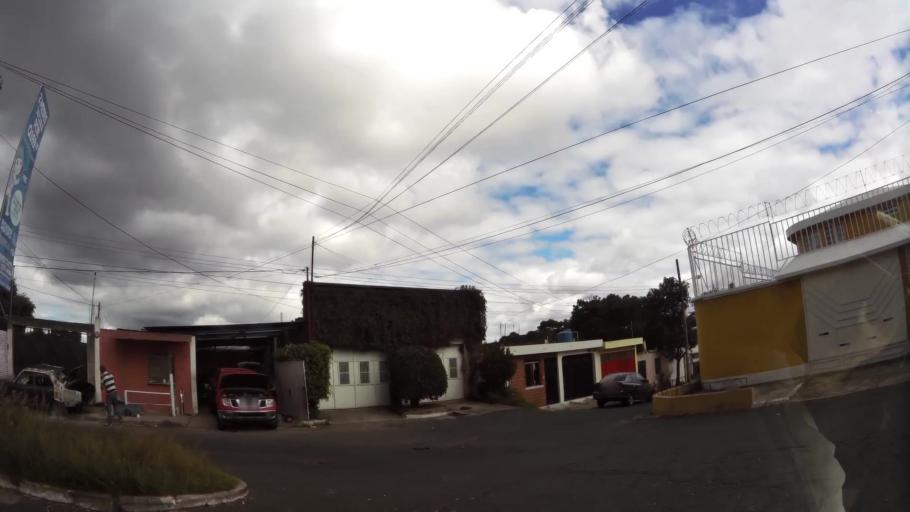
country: GT
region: Guatemala
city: Chinautla
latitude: 14.6859
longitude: -90.5481
